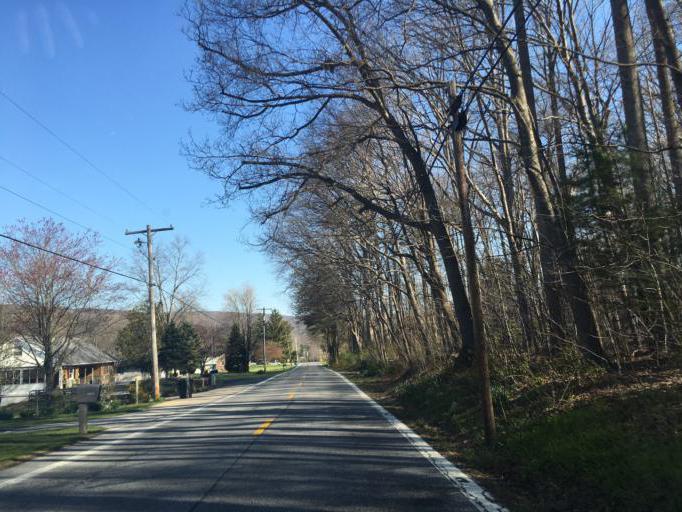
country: US
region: Maryland
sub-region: Washington County
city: Cavetown
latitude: 39.5868
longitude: -77.5574
